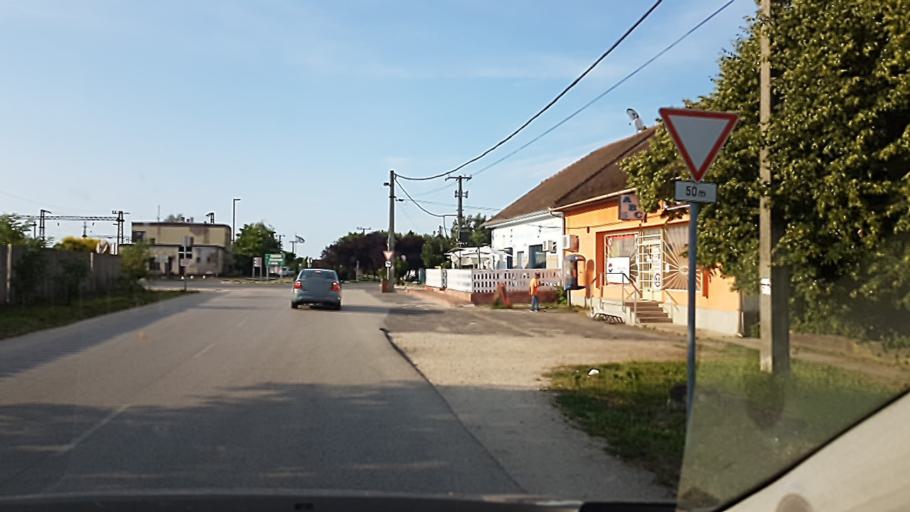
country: HU
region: Pest
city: Dunavarsany
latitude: 47.2525
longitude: 19.0611
